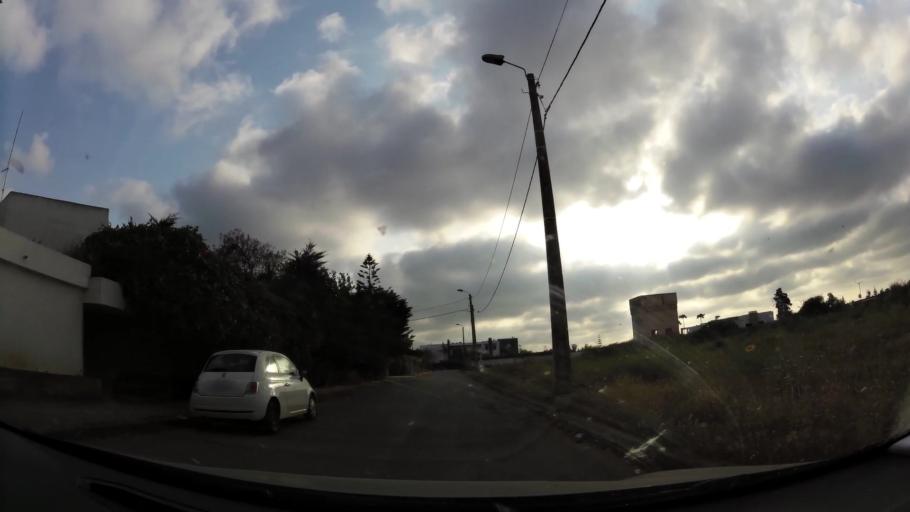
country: MA
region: Rabat-Sale-Zemmour-Zaer
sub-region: Rabat
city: Rabat
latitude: 33.9552
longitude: -6.8353
